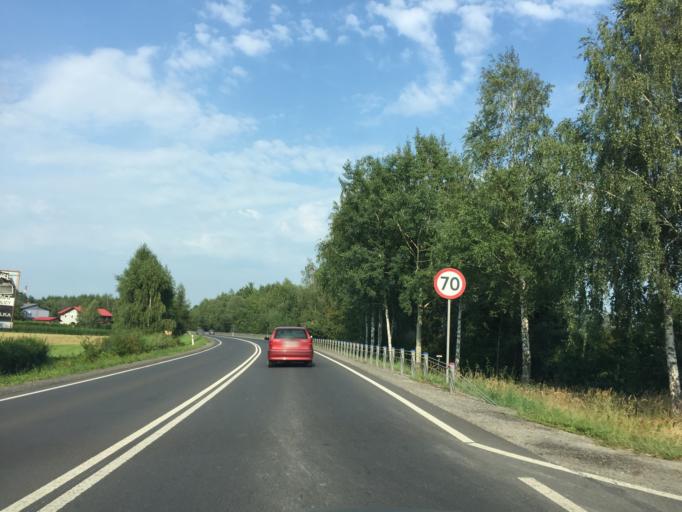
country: PL
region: Lesser Poland Voivodeship
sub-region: Powiat oswiecimski
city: Zaborze
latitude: 50.0210
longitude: 19.2471
